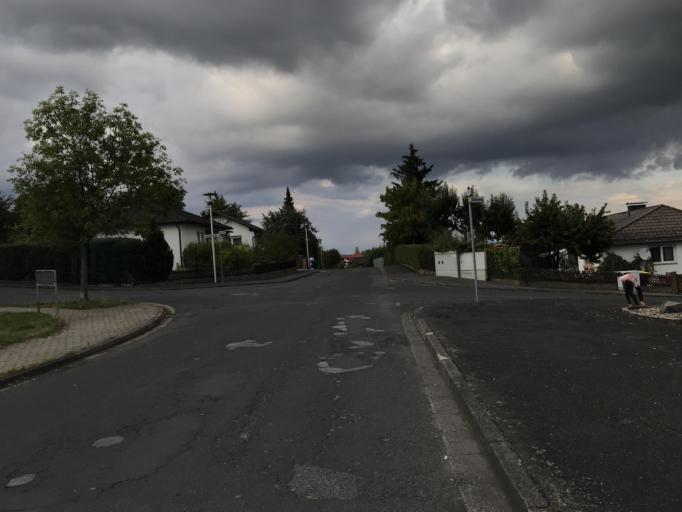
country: DE
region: Hesse
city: Borken
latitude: 51.0387
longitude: 9.2890
